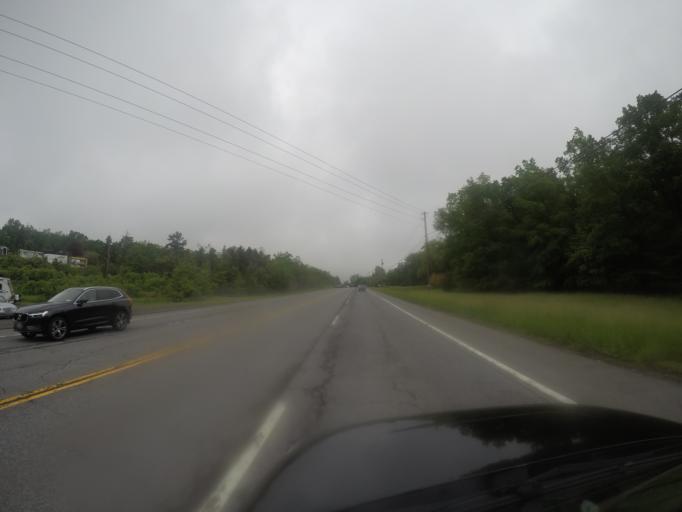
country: US
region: New York
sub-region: Ulster County
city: West Hurley
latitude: 41.9887
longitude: -74.0862
